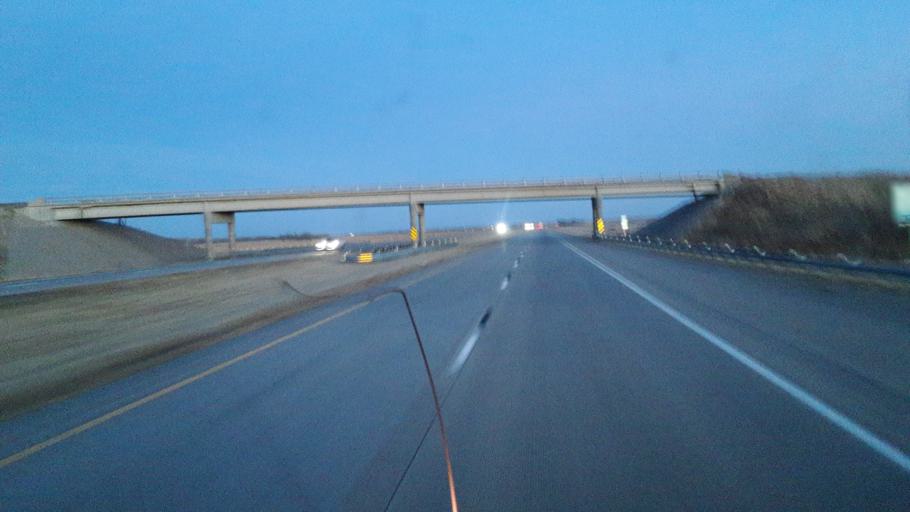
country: US
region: Nebraska
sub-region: Keith County
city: Ogallala
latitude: 41.1125
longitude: -101.5204
